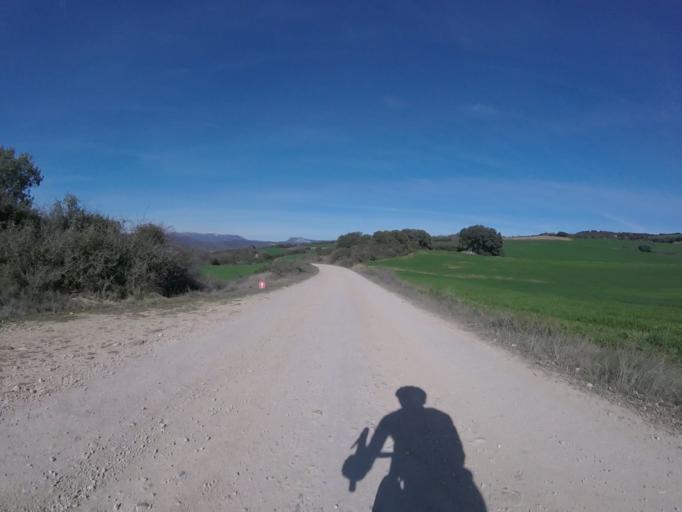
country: ES
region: Navarre
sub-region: Provincia de Navarra
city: Oteiza
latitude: 42.6432
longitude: -1.9585
